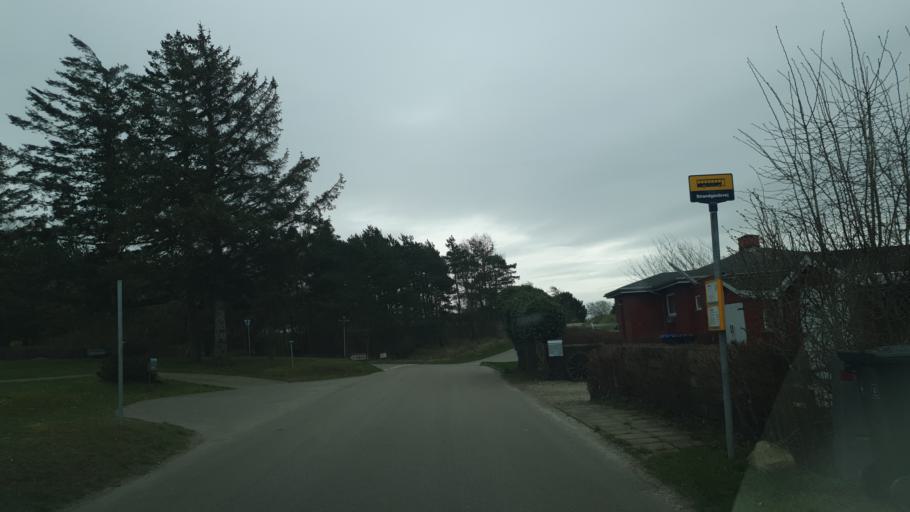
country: DK
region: Zealand
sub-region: Odsherred Kommune
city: Asnaes
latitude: 55.8383
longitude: 11.4513
